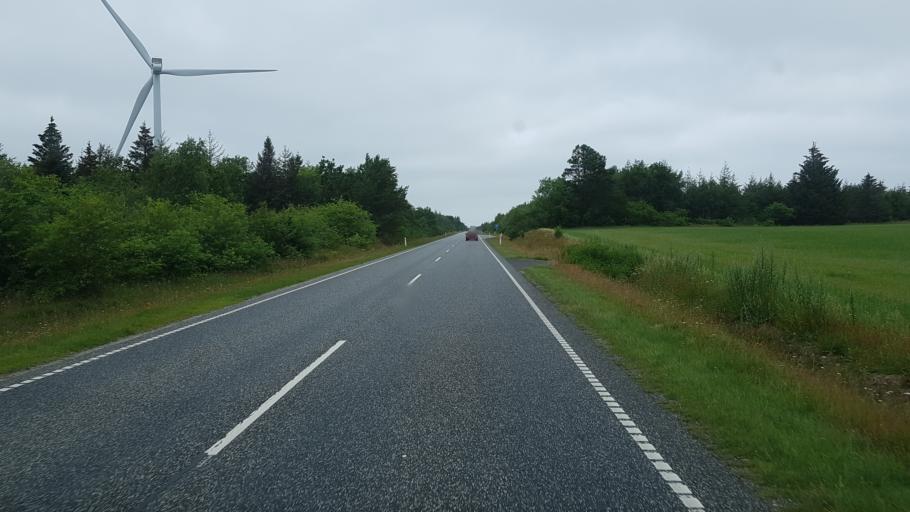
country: DK
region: Central Jutland
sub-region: Lemvig Kommune
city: Lemvig
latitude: 56.4482
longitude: 8.3528
